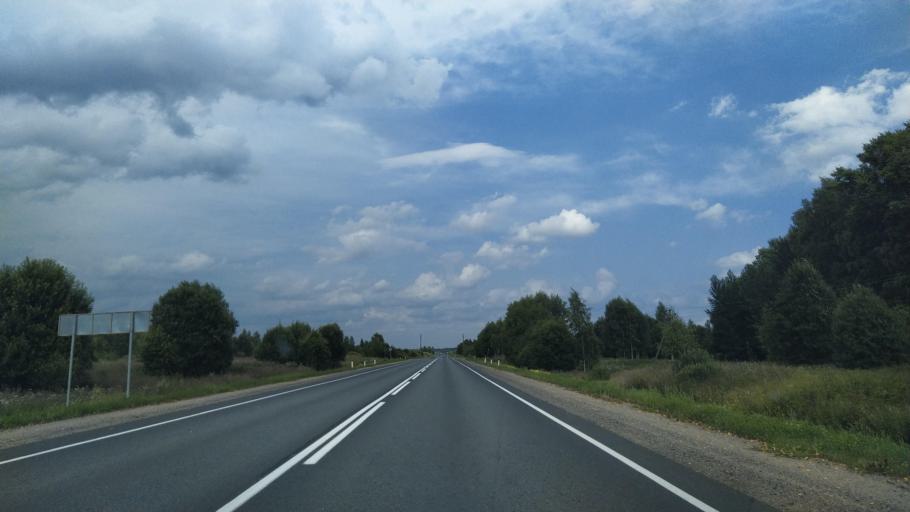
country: RU
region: Pskov
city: Porkhov
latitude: 57.9615
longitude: 29.6710
